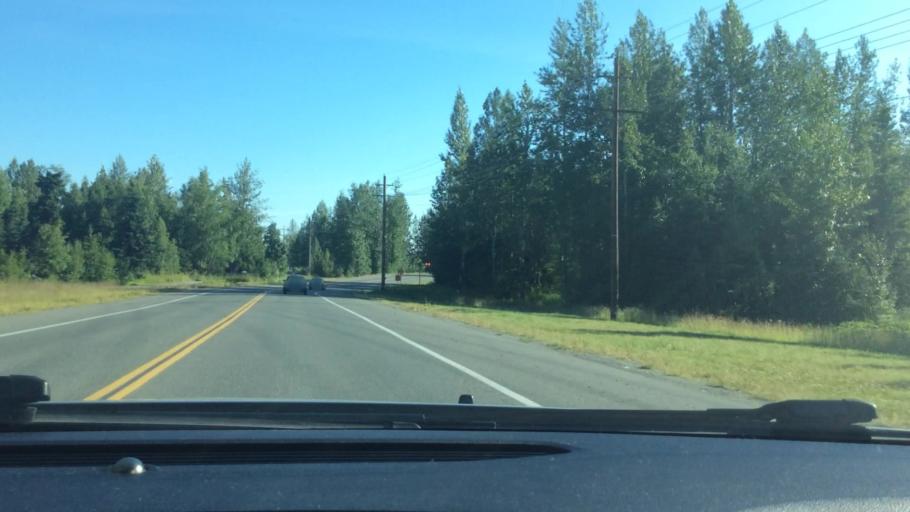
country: US
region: Alaska
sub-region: Anchorage Municipality
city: Elmendorf Air Force Base
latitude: 61.2436
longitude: -149.7059
